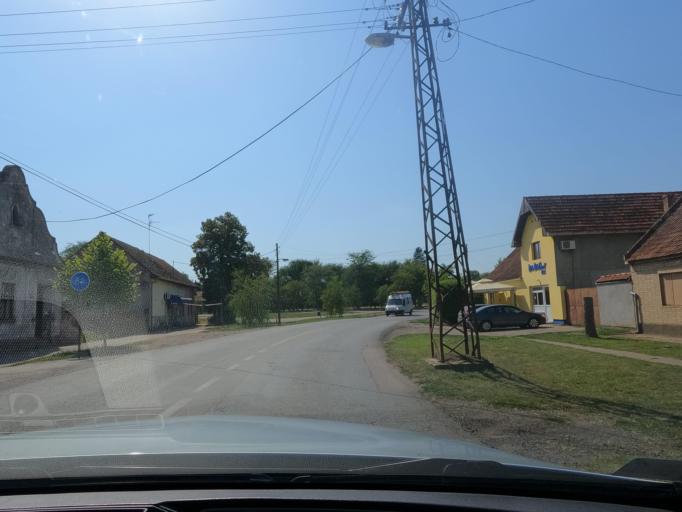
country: RS
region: Autonomna Pokrajina Vojvodina
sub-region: Severnobacki Okrug
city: Backa Topola
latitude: 45.8200
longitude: 19.6514
